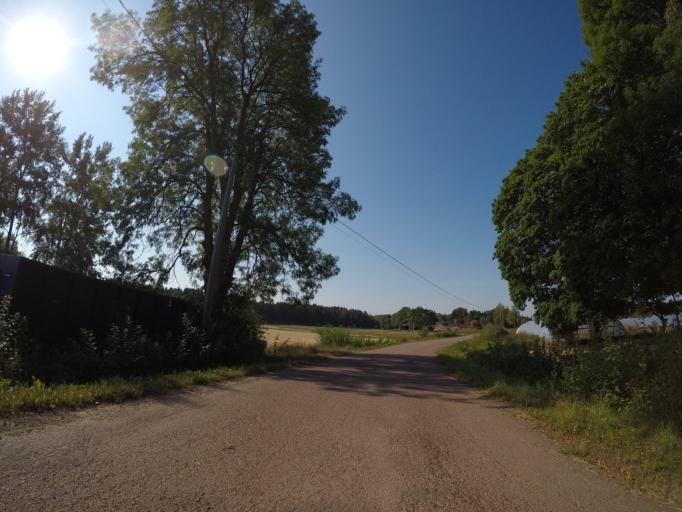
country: AX
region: Alands landsbygd
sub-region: Finstroem
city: Finstroem
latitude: 60.2716
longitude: 19.9400
